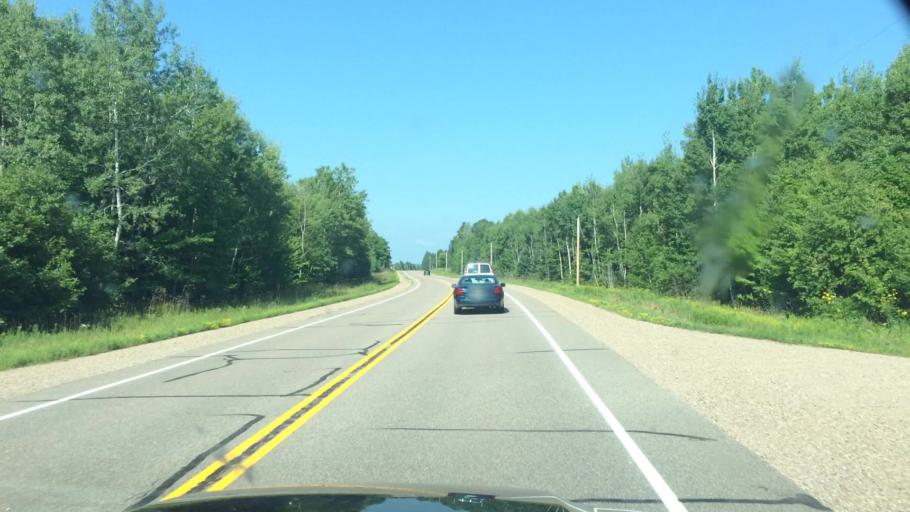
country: US
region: Wisconsin
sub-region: Langlade County
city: Antigo
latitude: 45.1483
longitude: -89.4169
